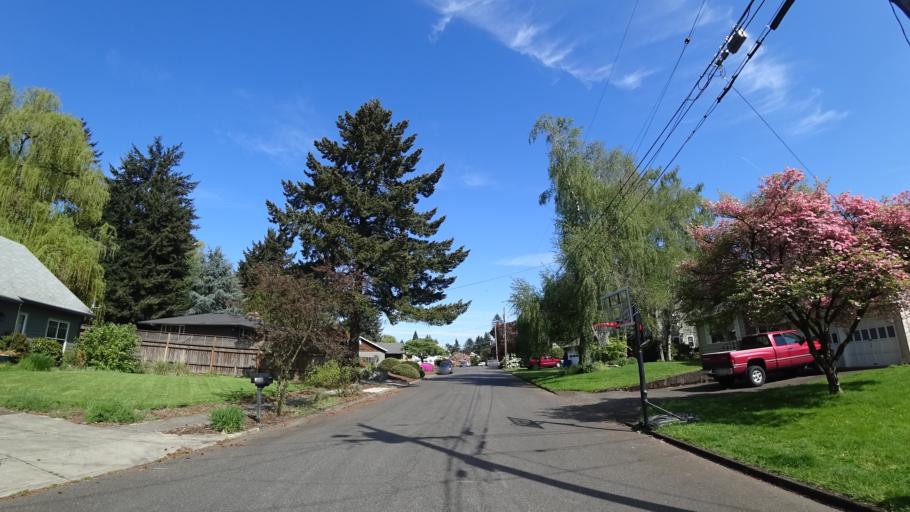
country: US
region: Oregon
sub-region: Clackamas County
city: Milwaukie
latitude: 45.4601
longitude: -122.6255
